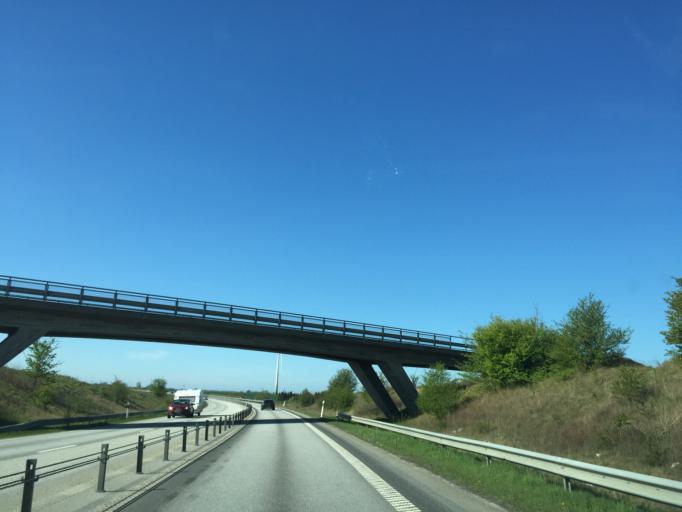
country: SE
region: Skane
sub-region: Staffanstorps Kommun
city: Hjaerup
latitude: 55.7057
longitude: 13.1427
